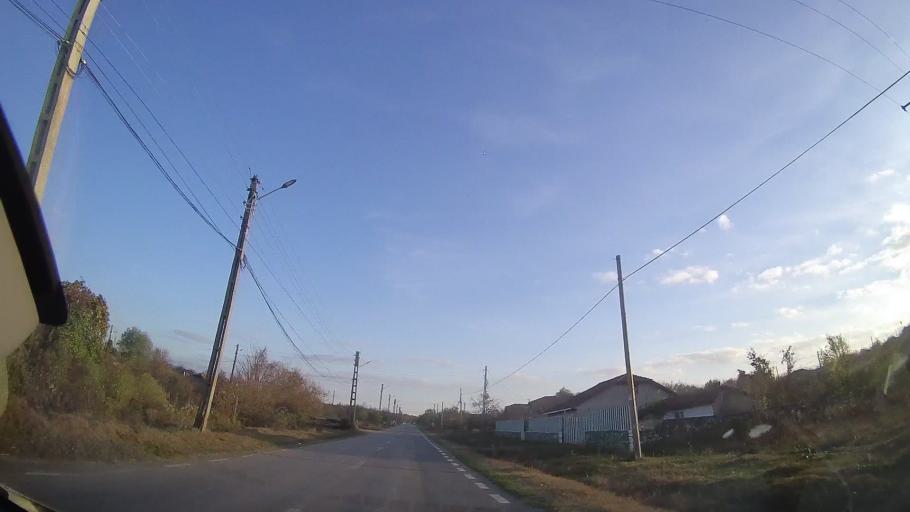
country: RO
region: Constanta
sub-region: Comuna Chirnogeni
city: Plopeni
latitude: 43.9504
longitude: 28.1978
